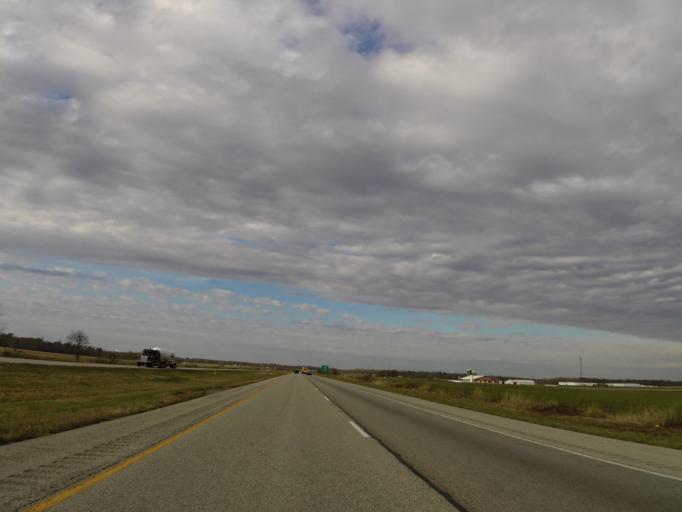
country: US
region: Illinois
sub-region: Washington County
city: Nashville
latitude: 38.3915
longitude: -89.3538
